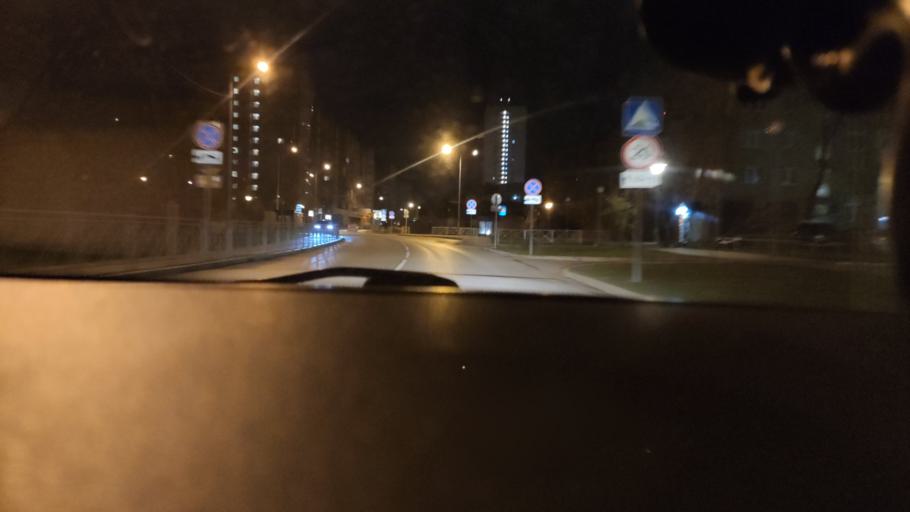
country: RU
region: Perm
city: Perm
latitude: 57.9803
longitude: 56.2008
